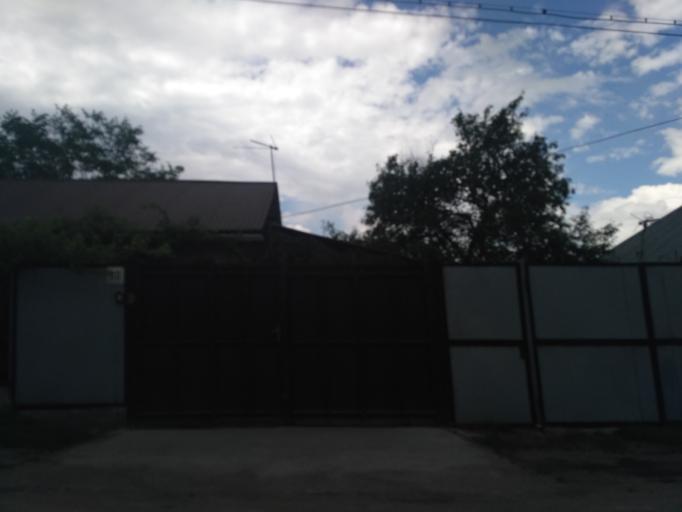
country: KZ
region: Almaty Oblysy
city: Burunday
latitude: 43.2040
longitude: 76.6358
